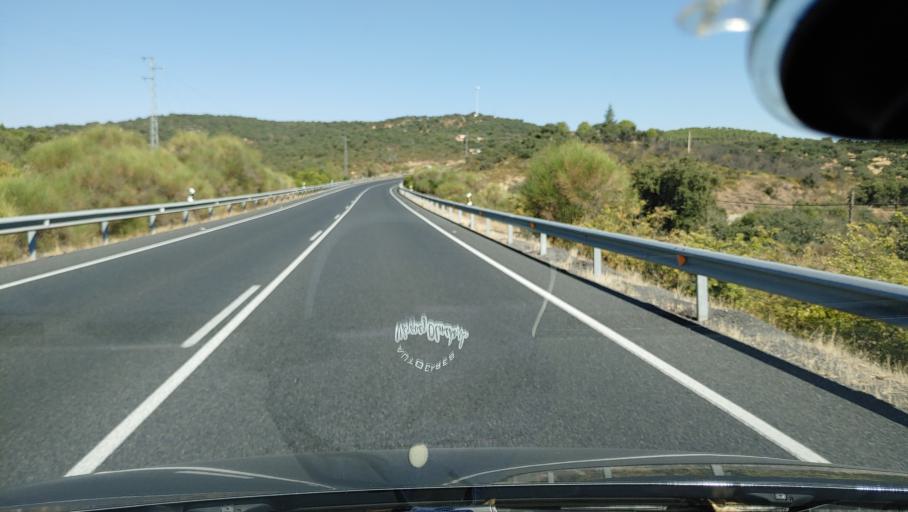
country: ES
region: Andalusia
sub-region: Province of Cordoba
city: Villaharta
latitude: 38.1020
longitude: -4.8768
